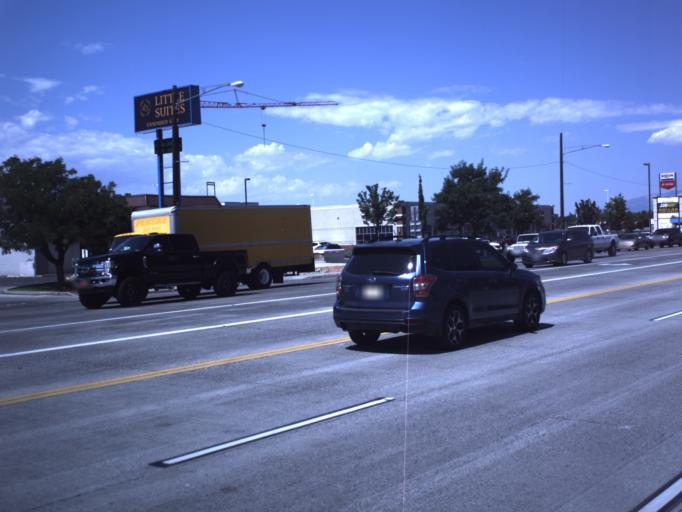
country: US
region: Utah
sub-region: Utah County
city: Provo
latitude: 40.2152
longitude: -111.6588
